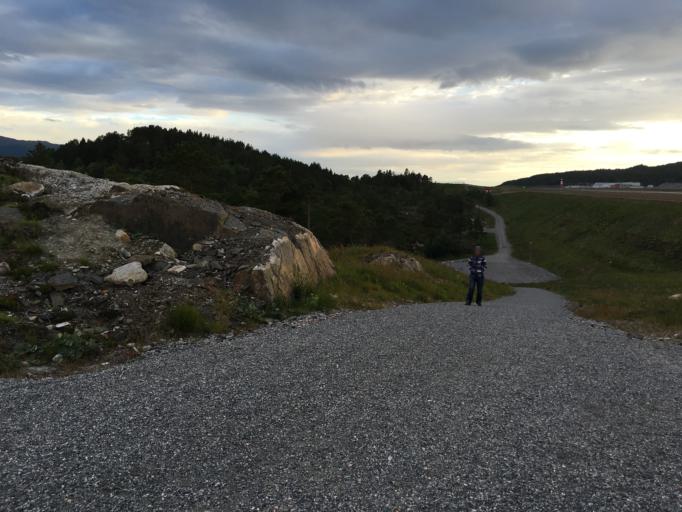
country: NO
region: More og Romsdal
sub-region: Kristiansund
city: Rensvik
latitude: 63.1146
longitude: 7.8522
